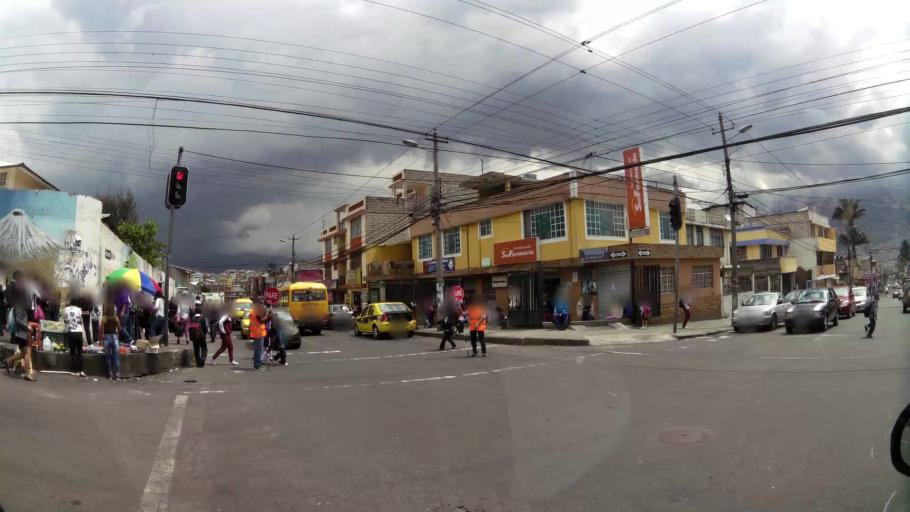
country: EC
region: Pichincha
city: Quito
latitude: -0.2543
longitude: -78.5156
